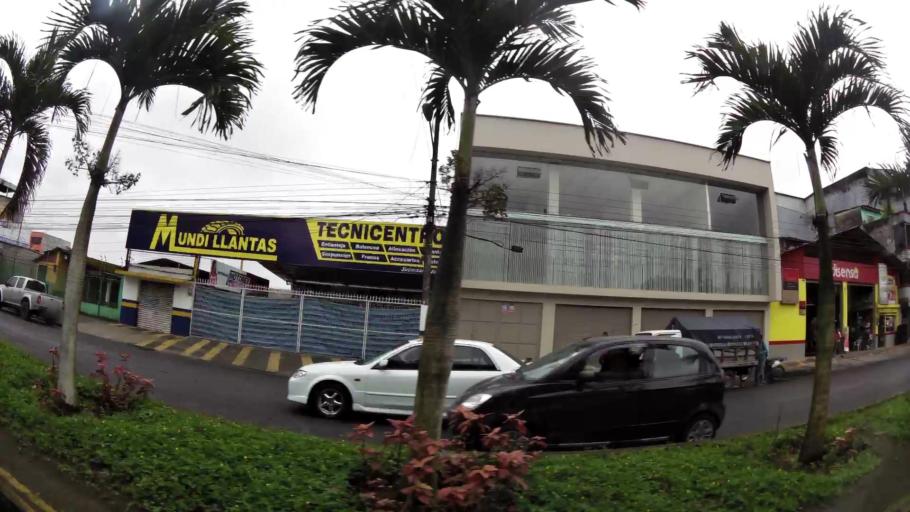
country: EC
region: Santo Domingo de los Tsachilas
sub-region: Canton Santo Domingo de los Colorados
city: Santo Domingo de los Colorados
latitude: -0.2591
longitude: -79.1820
